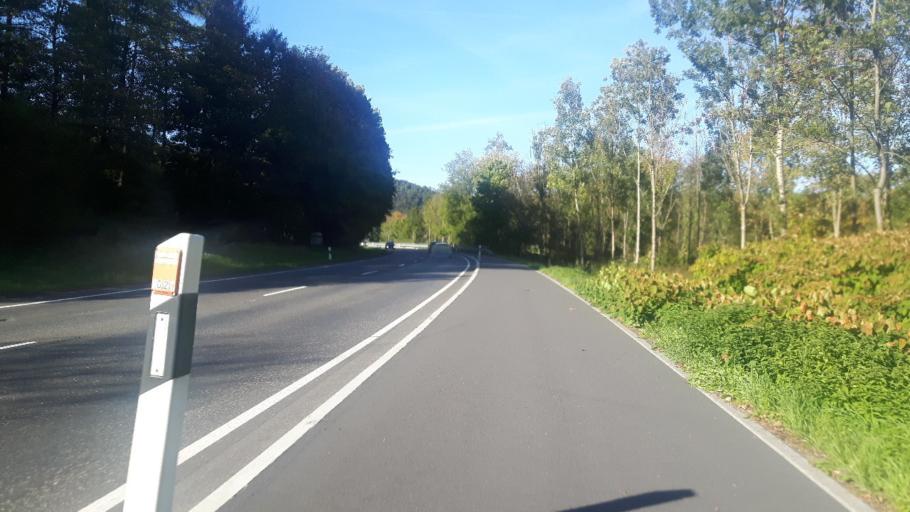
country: DE
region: Rheinland-Pfalz
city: Mittelhof
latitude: 50.7910
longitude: 7.7927
